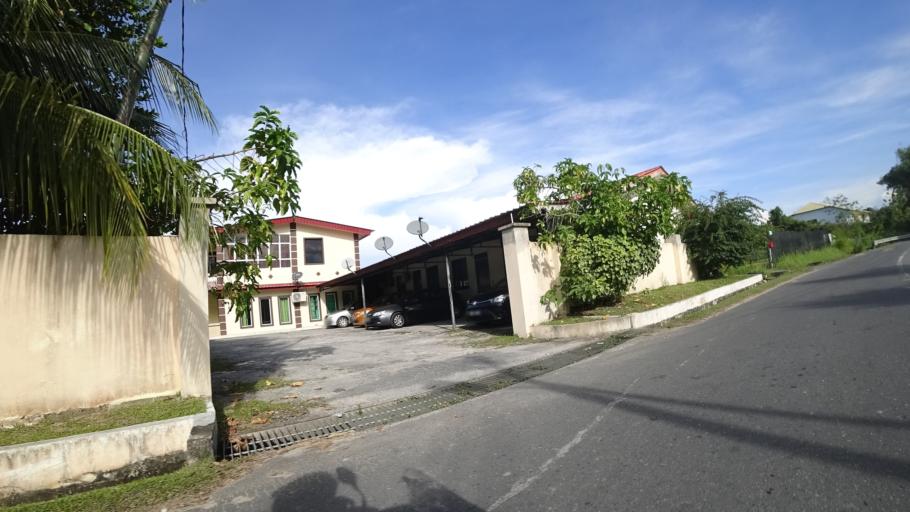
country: BN
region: Brunei and Muara
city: Bandar Seri Begawan
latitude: 4.8968
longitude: 114.8445
